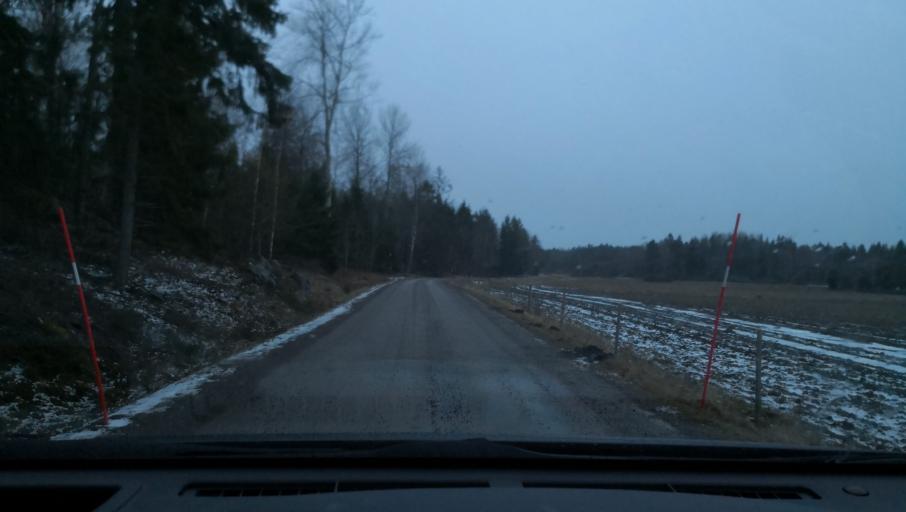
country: SE
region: Uppsala
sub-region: Enkopings Kommun
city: Hummelsta
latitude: 59.4649
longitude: 16.8304
